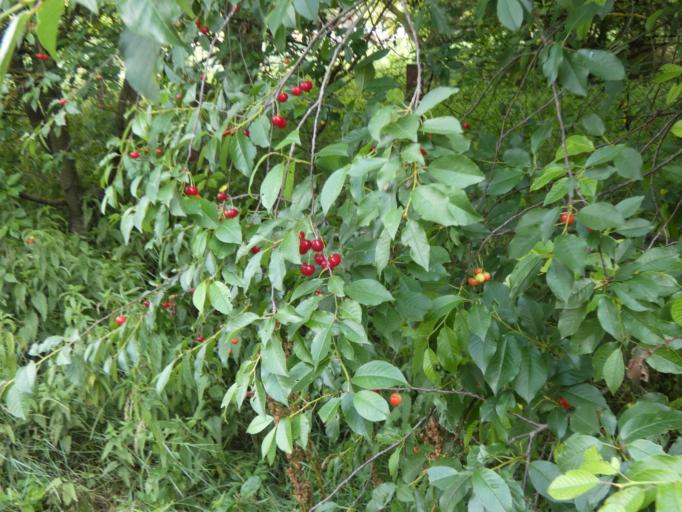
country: HU
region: Pest
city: Mende
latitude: 47.4059
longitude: 19.4840
